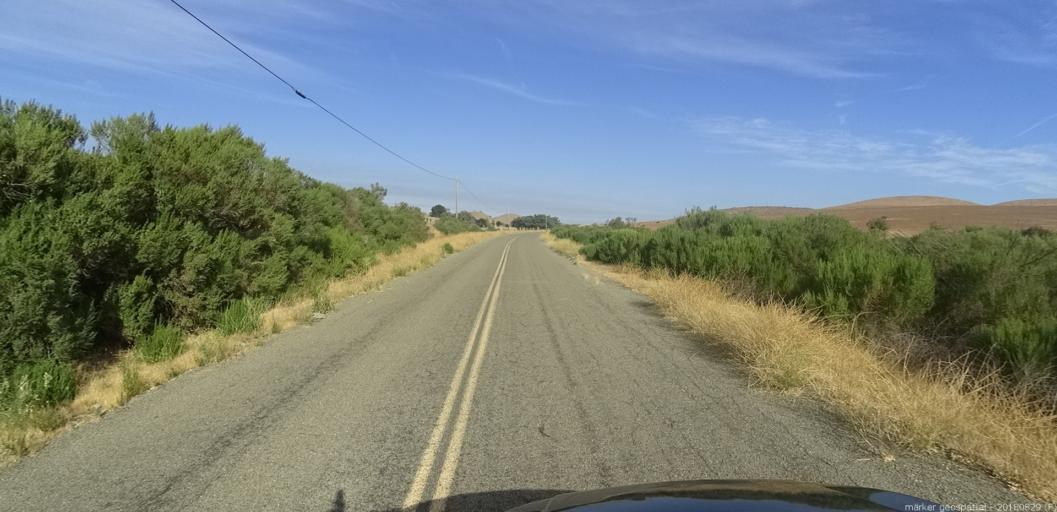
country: US
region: California
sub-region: Monterey County
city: King City
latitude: 36.0363
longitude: -120.9652
